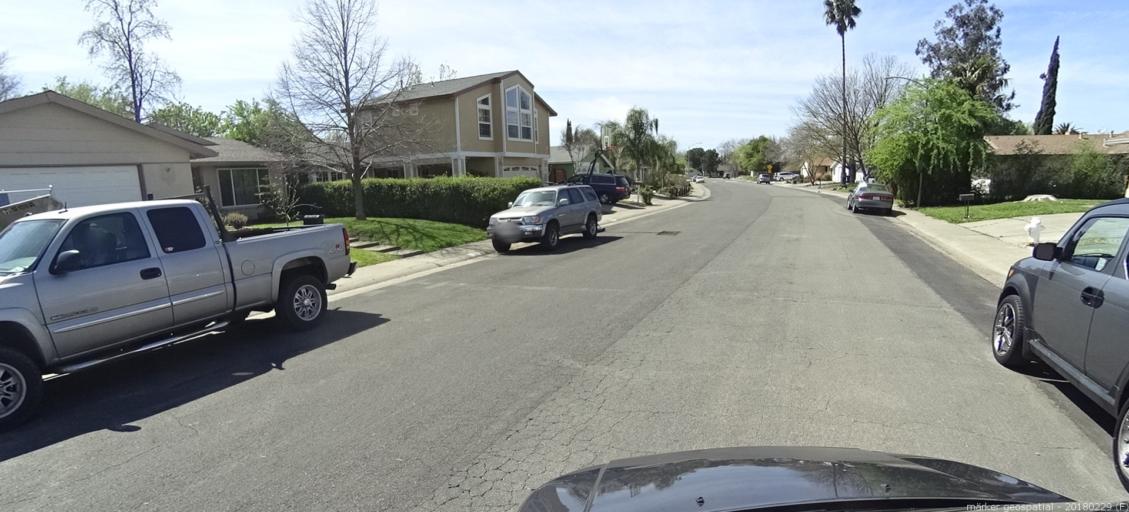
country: US
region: California
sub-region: Sacramento County
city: Rosemont
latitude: 38.5406
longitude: -121.3467
